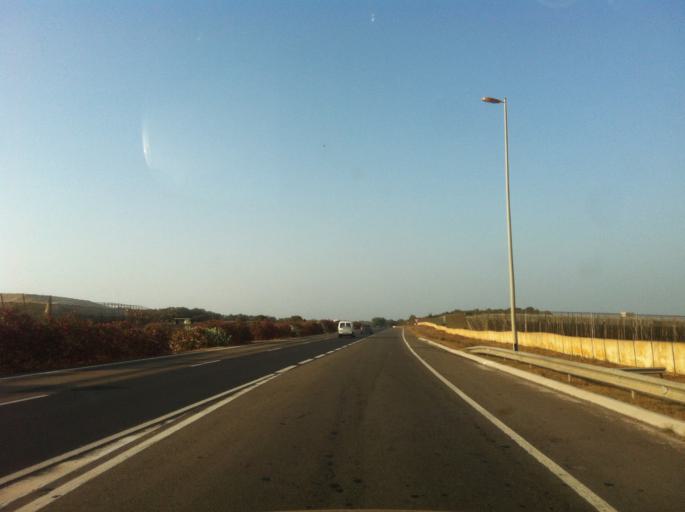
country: MA
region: Gharb-Chrarda-Beni Hssen
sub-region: Kenitra Province
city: Kenitra
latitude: 34.4146
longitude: -6.5235
